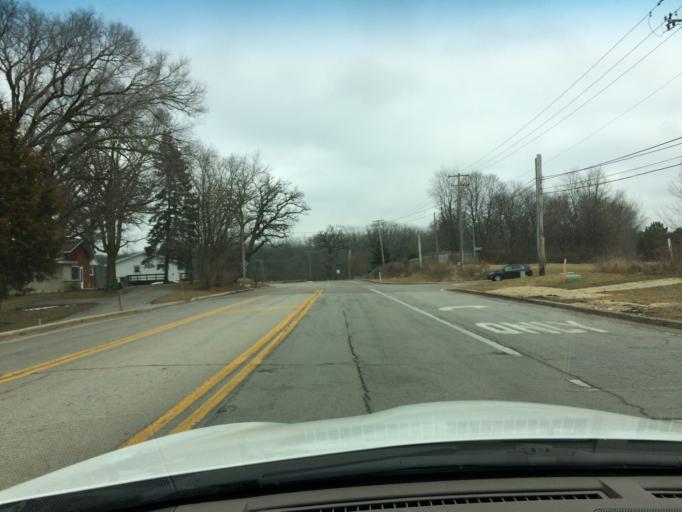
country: US
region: Illinois
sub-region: Kane County
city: Sugar Grove
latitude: 41.7789
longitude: -88.4419
